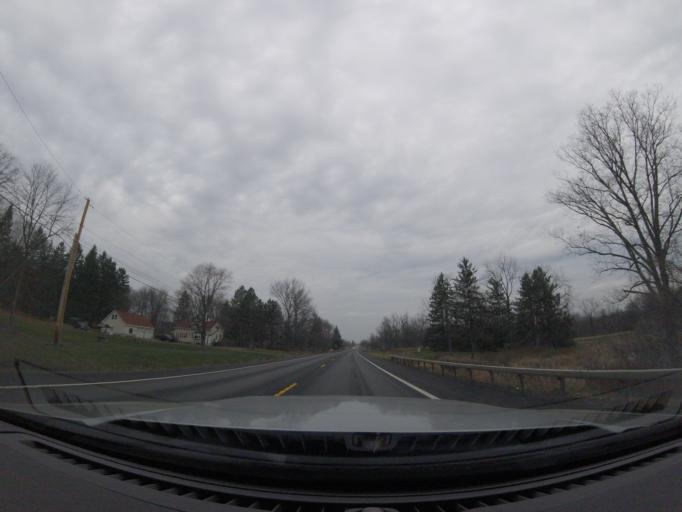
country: US
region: New York
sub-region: Schuyler County
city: Watkins Glen
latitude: 42.4309
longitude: -76.9069
